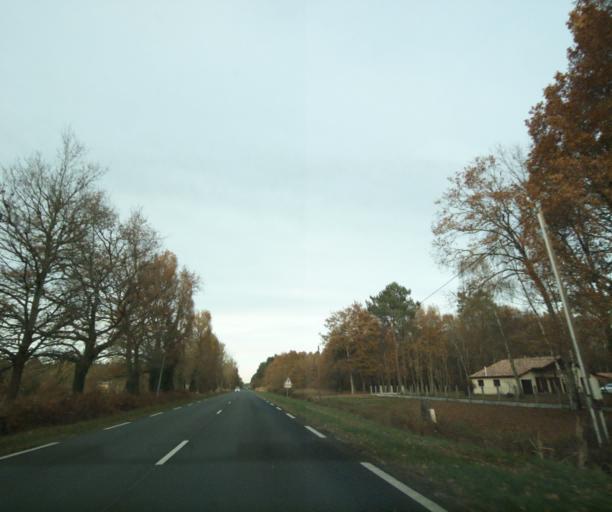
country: FR
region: Aquitaine
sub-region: Departement de la Gironde
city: Bazas
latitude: 44.3014
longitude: -0.2558
